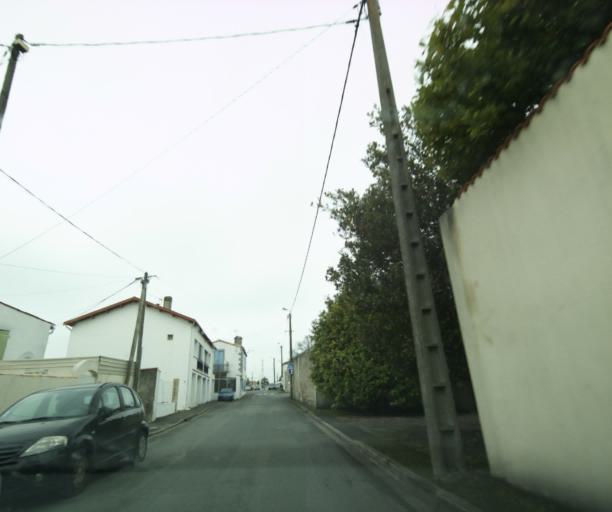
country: FR
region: Poitou-Charentes
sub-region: Departement de la Charente-Maritime
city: La Rochelle
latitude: 46.1770
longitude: -1.1409
